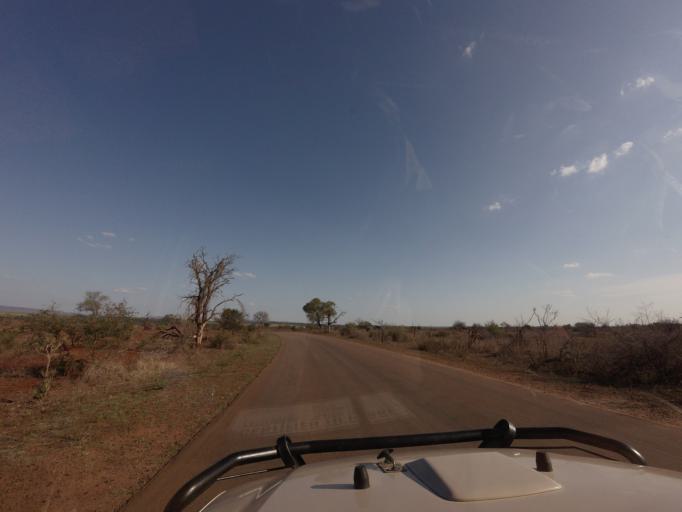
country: ZA
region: Mpumalanga
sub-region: Ehlanzeni District
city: Komatipoort
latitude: -25.3497
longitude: 31.8845
